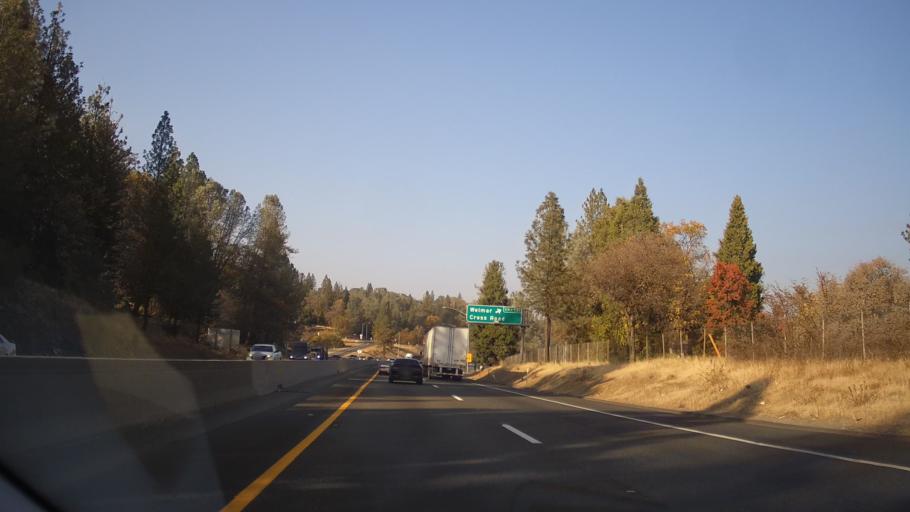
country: US
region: California
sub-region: Placer County
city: Meadow Vista
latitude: 39.0406
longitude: -120.9735
